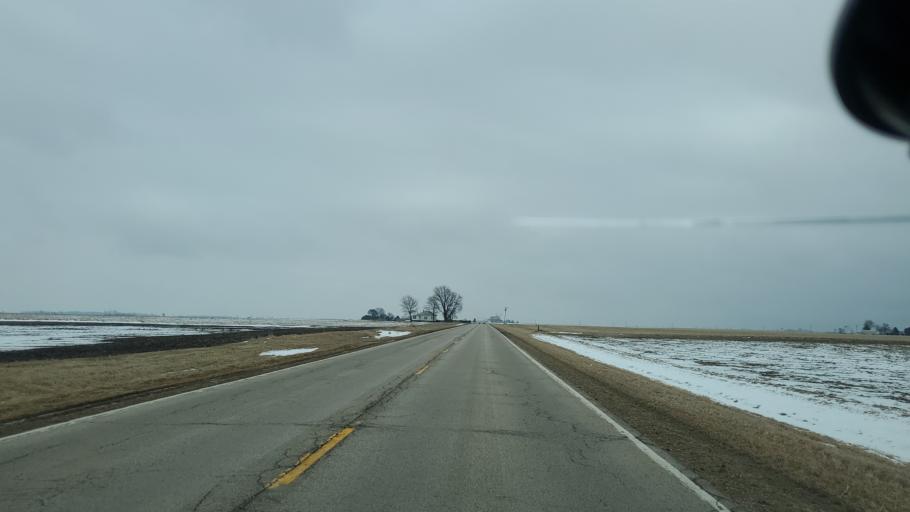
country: US
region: Illinois
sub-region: Marshall County
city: Wenona
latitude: 41.1188
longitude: -89.1161
